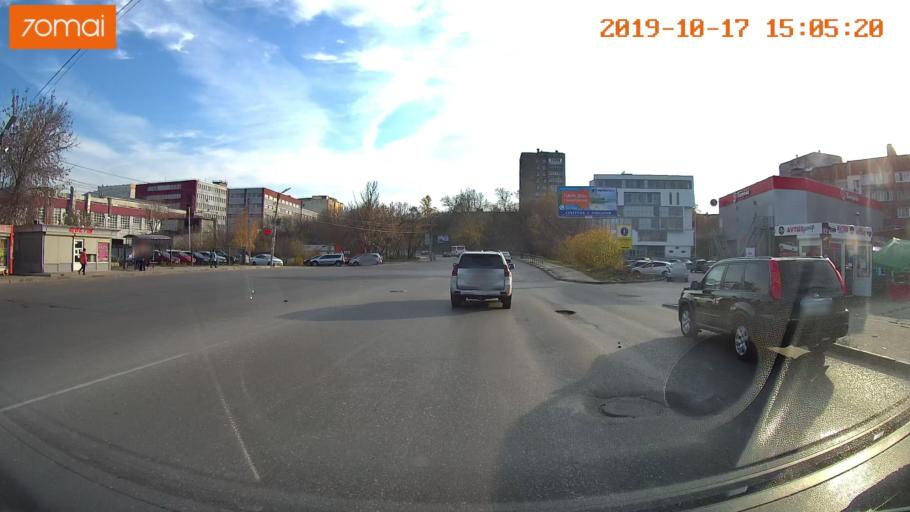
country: RU
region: Rjazan
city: Ryazan'
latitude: 54.6367
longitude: 39.7230
